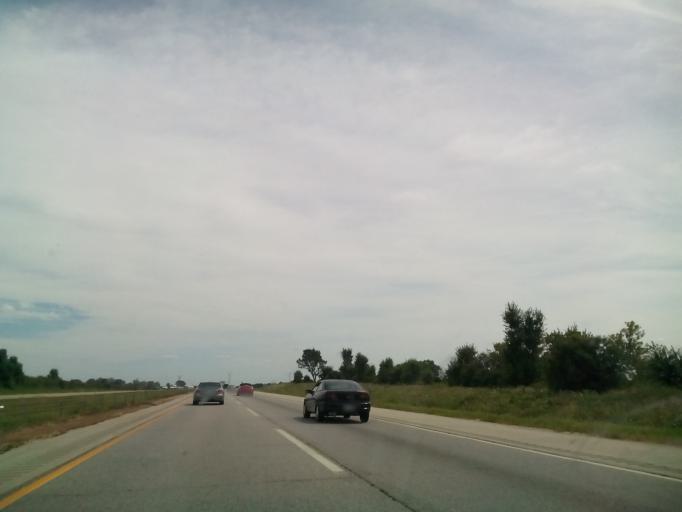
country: US
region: Illinois
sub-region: Kane County
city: Sugar Grove
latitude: 41.8144
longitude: -88.4525
